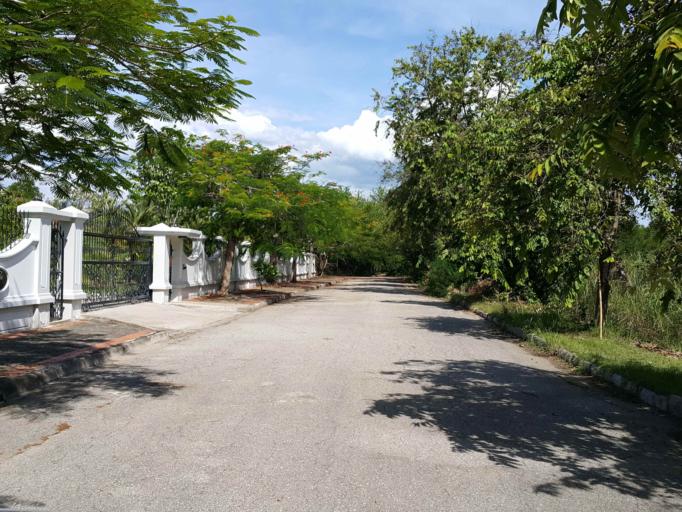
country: TH
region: Chiang Mai
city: San Kamphaeng
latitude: 18.7578
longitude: 99.1169
